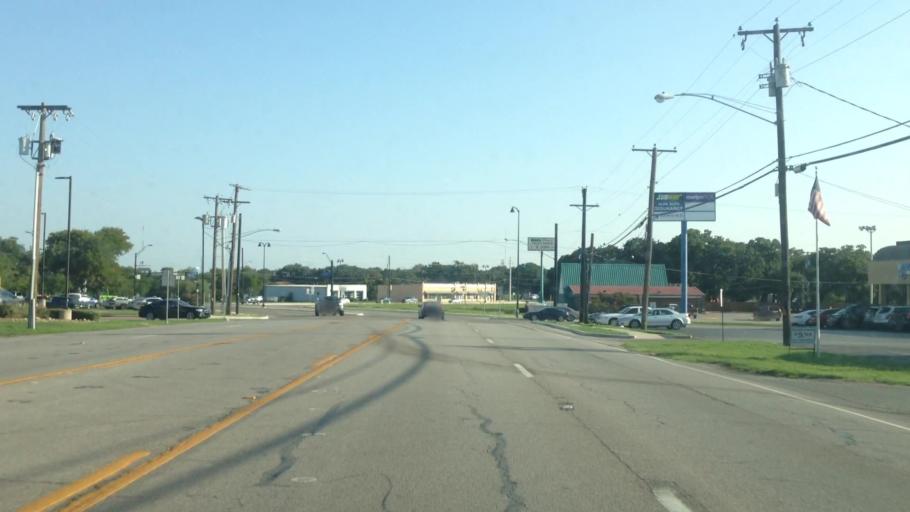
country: US
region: Texas
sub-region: Tarrant County
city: Haltom City
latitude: 32.8031
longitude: -97.2646
